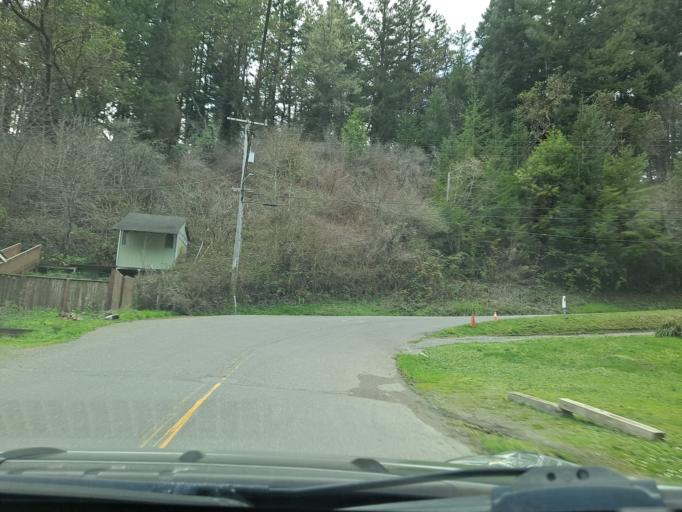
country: US
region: California
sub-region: Humboldt County
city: Fortuna
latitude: 40.6039
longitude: -124.1612
